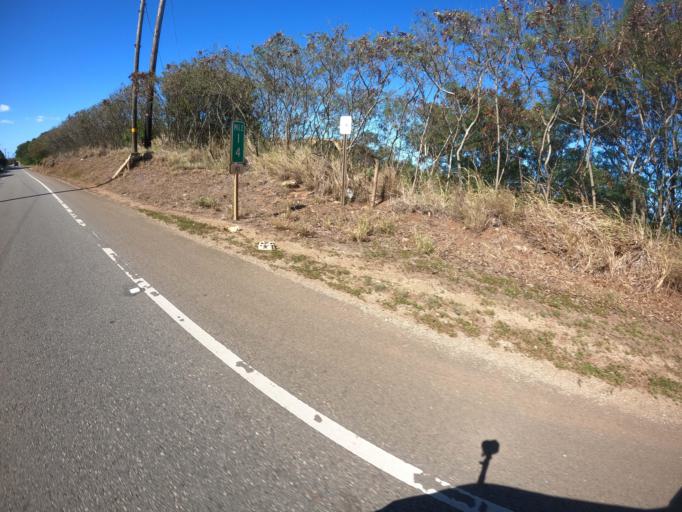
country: US
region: Hawaii
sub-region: Honolulu County
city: Kahuku
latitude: 21.6900
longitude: -157.9687
